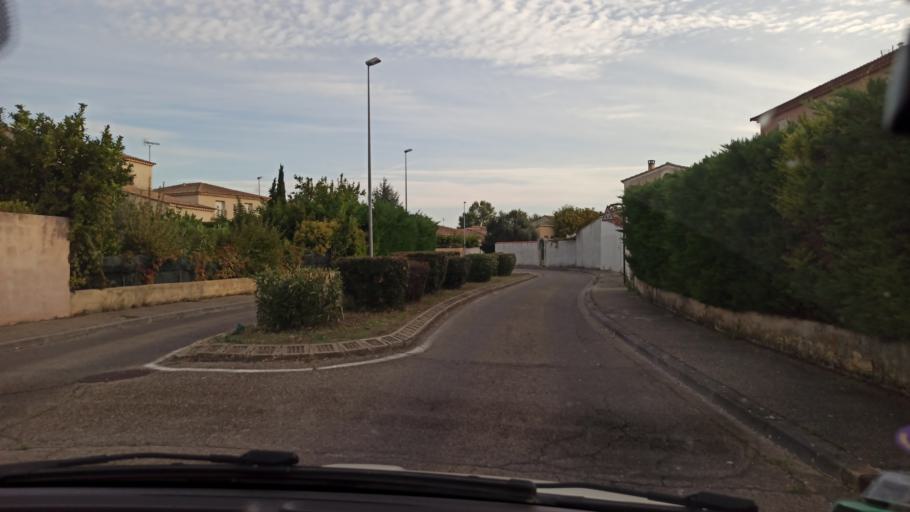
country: FR
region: Provence-Alpes-Cote d'Azur
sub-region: Departement du Vaucluse
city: Le Pontet
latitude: 43.9397
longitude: 4.8476
